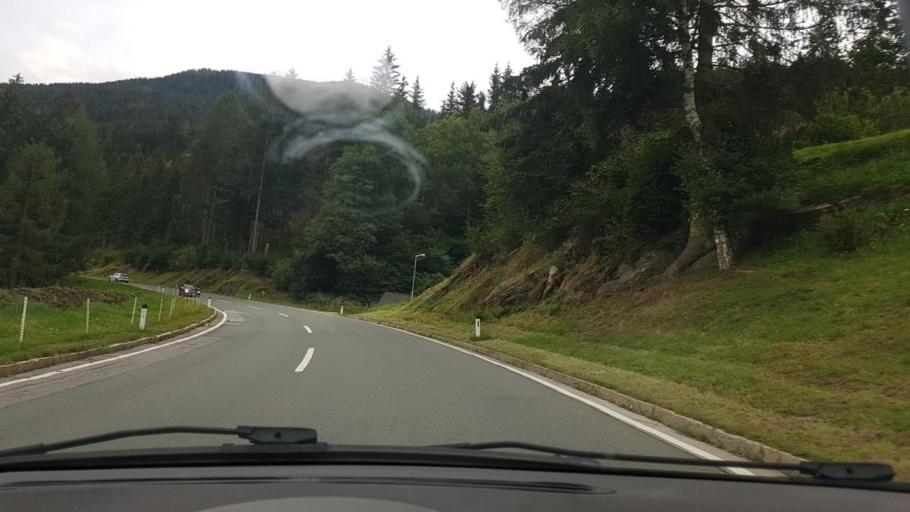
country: AT
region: Carinthia
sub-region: Politischer Bezirk Spittal an der Drau
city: Winklern
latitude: 46.8645
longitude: 12.8744
